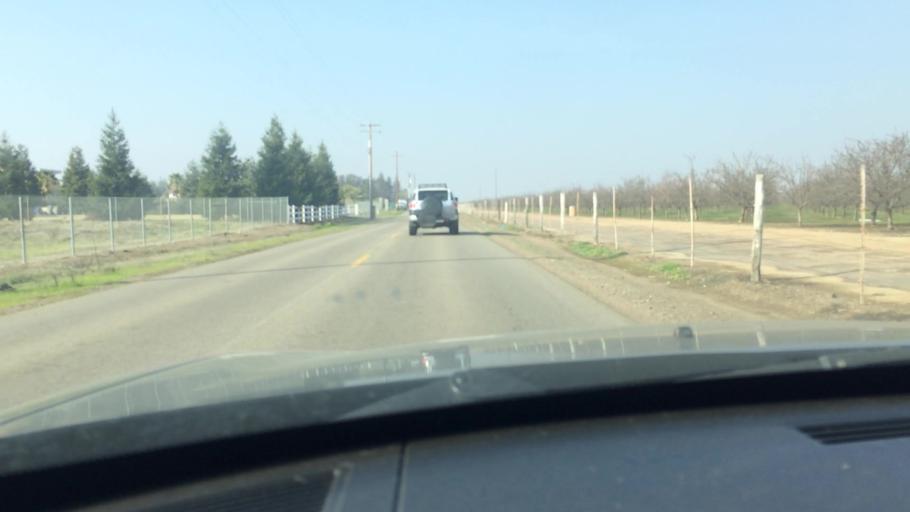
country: US
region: California
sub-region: Fresno County
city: Clovis
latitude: 36.8811
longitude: -119.6949
